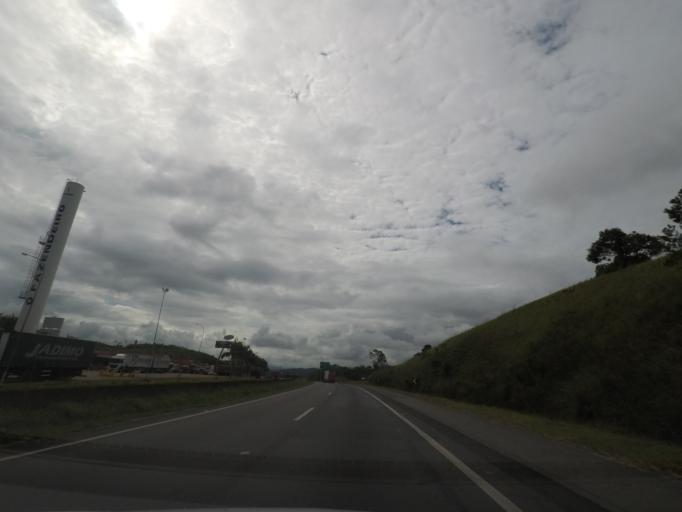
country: BR
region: Sao Paulo
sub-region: Miracatu
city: Miracatu
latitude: -24.2605
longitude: -47.3772
